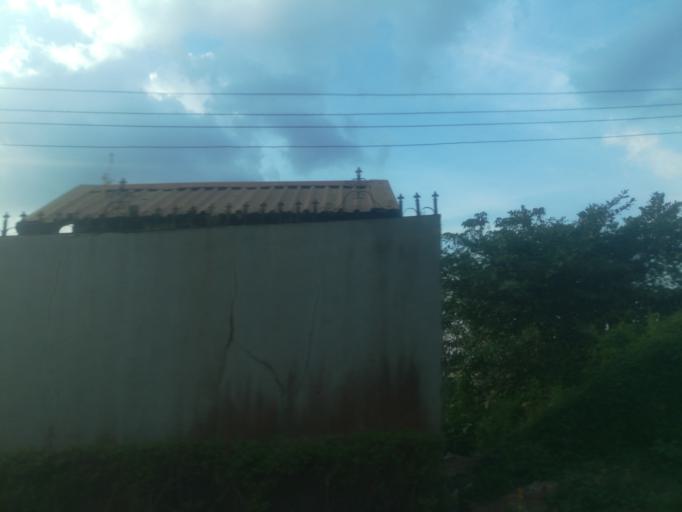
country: NG
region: Ogun
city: Abeokuta
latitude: 7.1305
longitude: 3.3212
